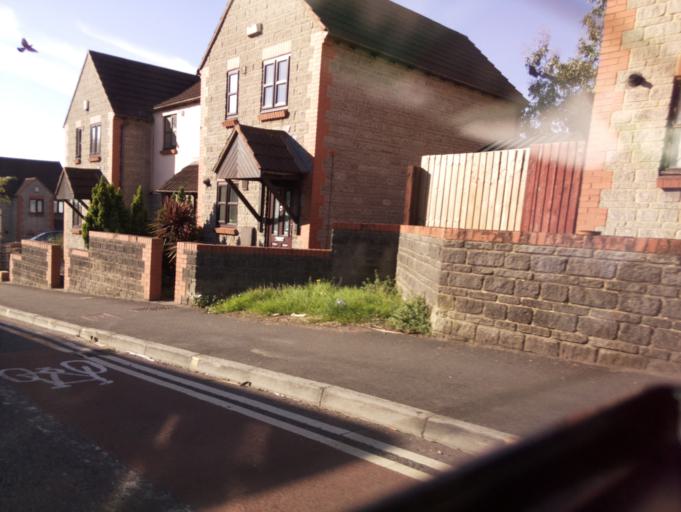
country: GB
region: England
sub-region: South Gloucestershire
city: Kingswood
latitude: 51.4514
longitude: -2.5216
